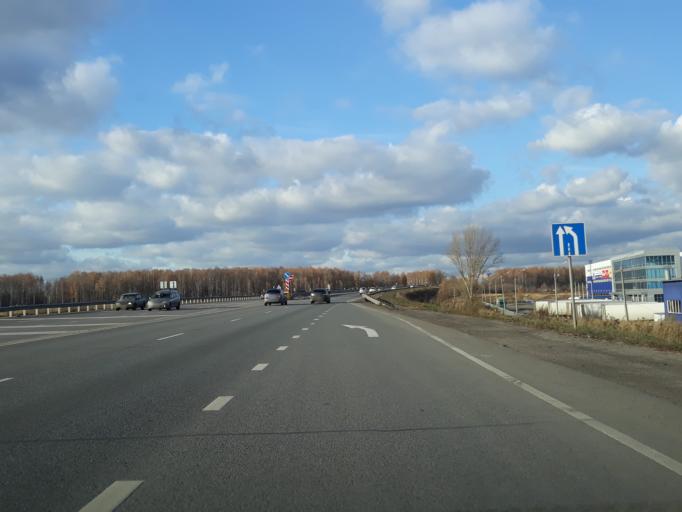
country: RU
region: Nizjnij Novgorod
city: Afonino
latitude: 56.2118
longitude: 44.0818
